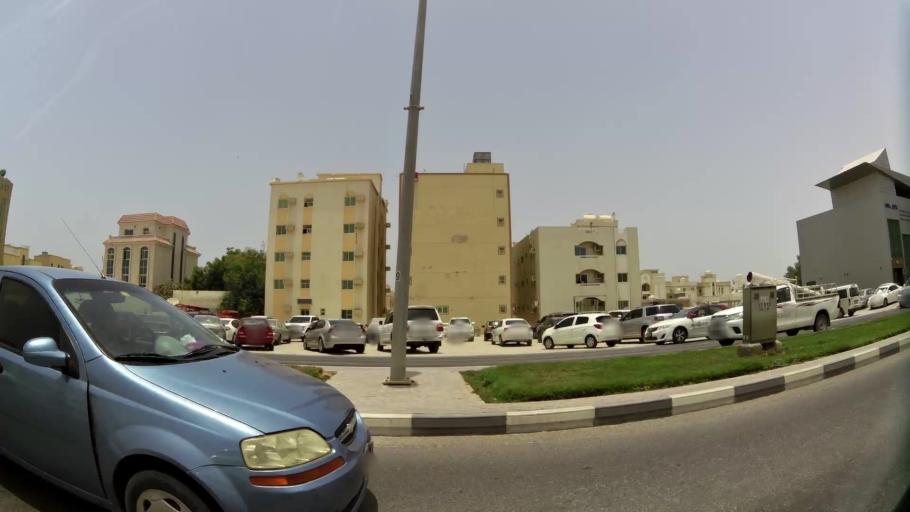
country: AE
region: Ash Shariqah
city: Sharjah
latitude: 25.3548
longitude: 55.3987
